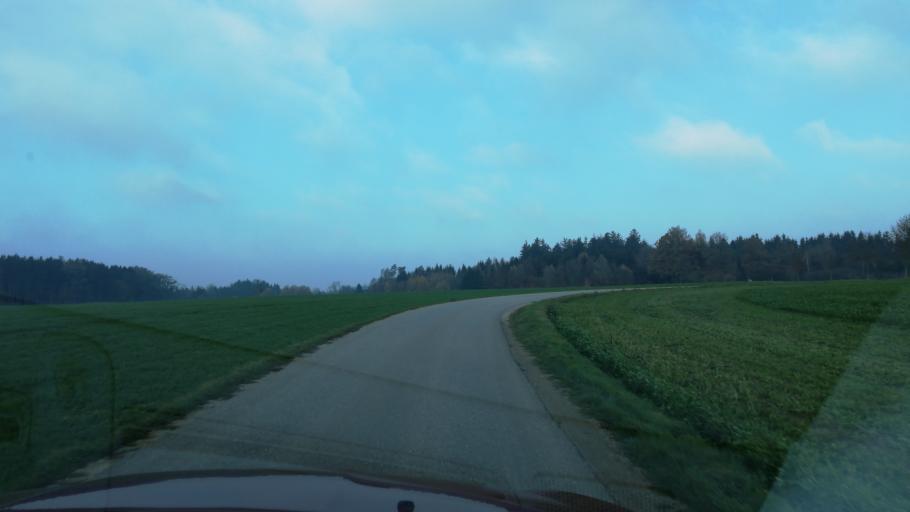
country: AT
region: Upper Austria
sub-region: Politischer Bezirk Kirchdorf an der Krems
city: Kremsmunster
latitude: 48.1042
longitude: 14.1757
